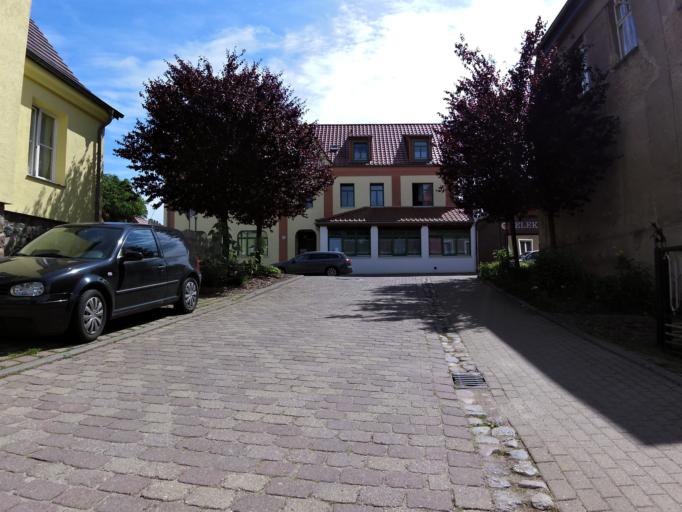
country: DE
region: Mecklenburg-Vorpommern
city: Loitz
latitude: 53.3335
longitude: 13.4364
